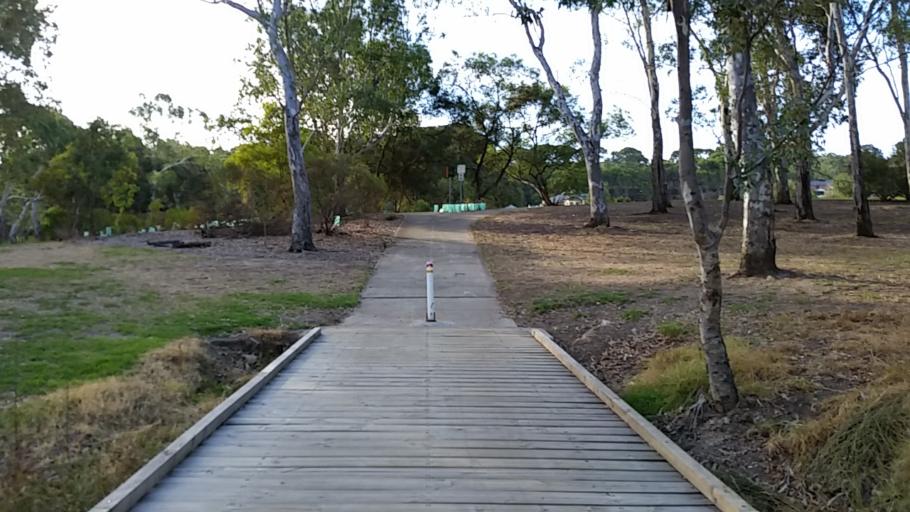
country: AU
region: South Australia
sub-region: Campbelltown
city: Athelstone
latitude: -34.8606
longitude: 138.7075
